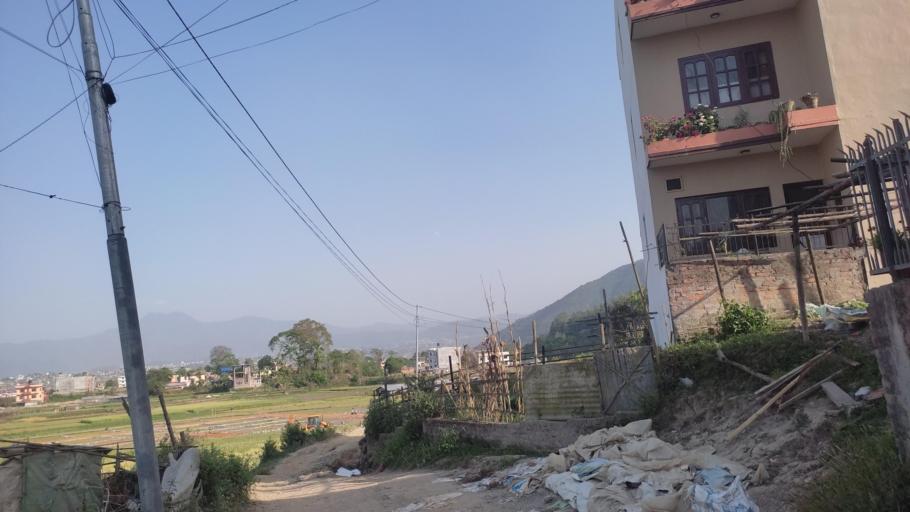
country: NP
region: Central Region
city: Kirtipur
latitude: 27.6579
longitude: 85.2710
